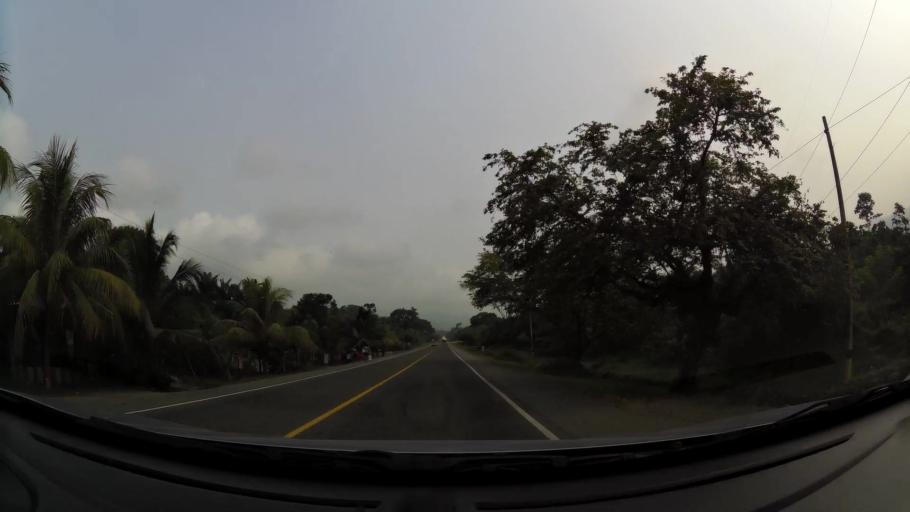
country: HN
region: Atlantida
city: Mezapa
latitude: 15.6108
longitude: -87.6134
